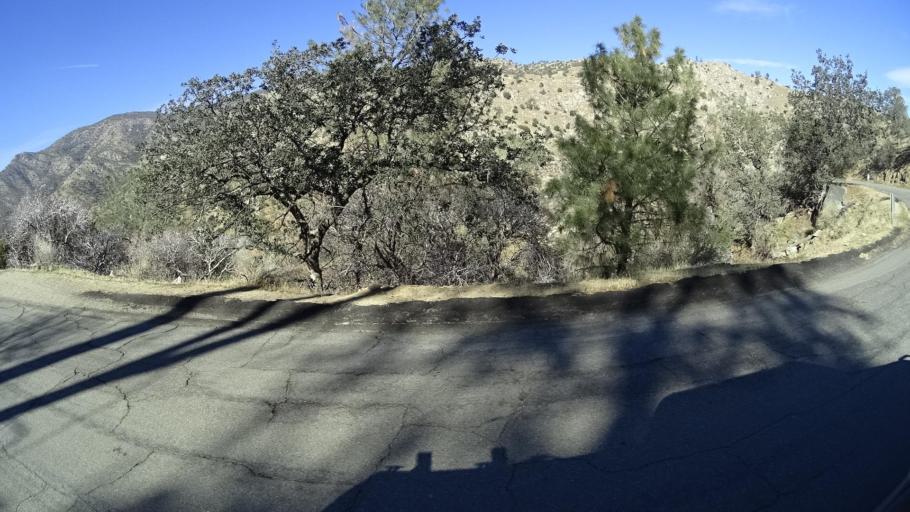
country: US
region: California
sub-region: Kern County
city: Bodfish
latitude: 35.5750
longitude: -118.5426
